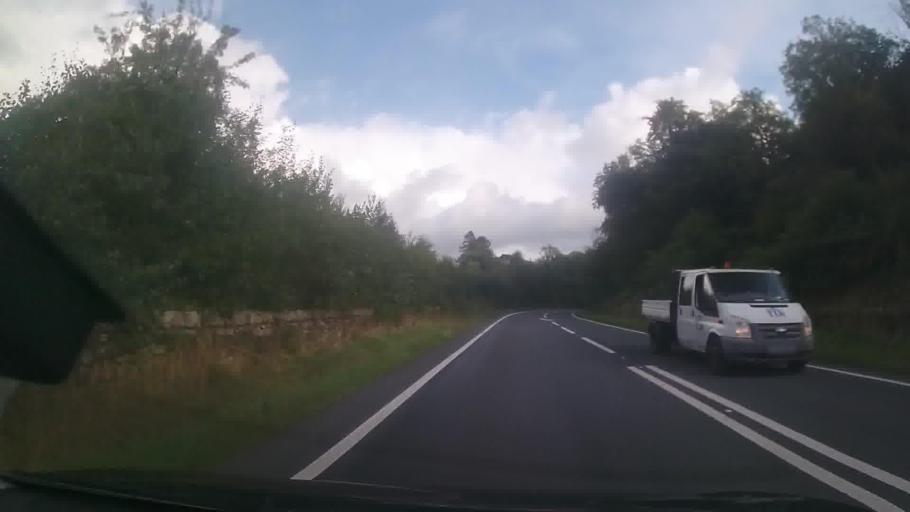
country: GB
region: Wales
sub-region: Gwynedd
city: Dolgellau
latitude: 52.7486
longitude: -3.8443
